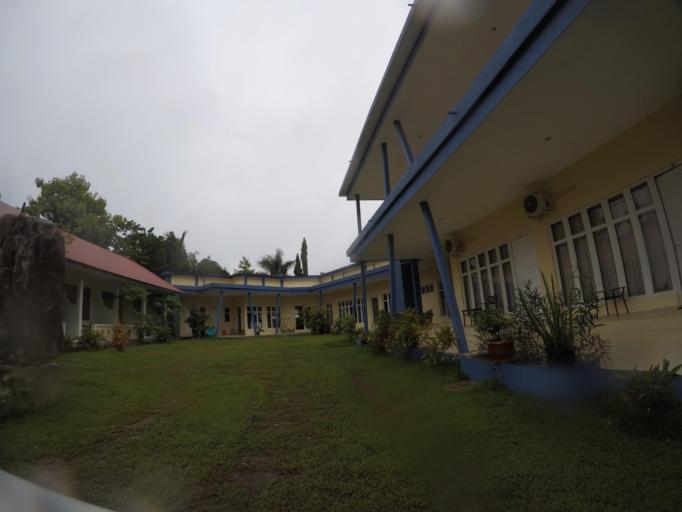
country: TL
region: Bobonaro
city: Maliana
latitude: -8.9946
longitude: 125.2265
